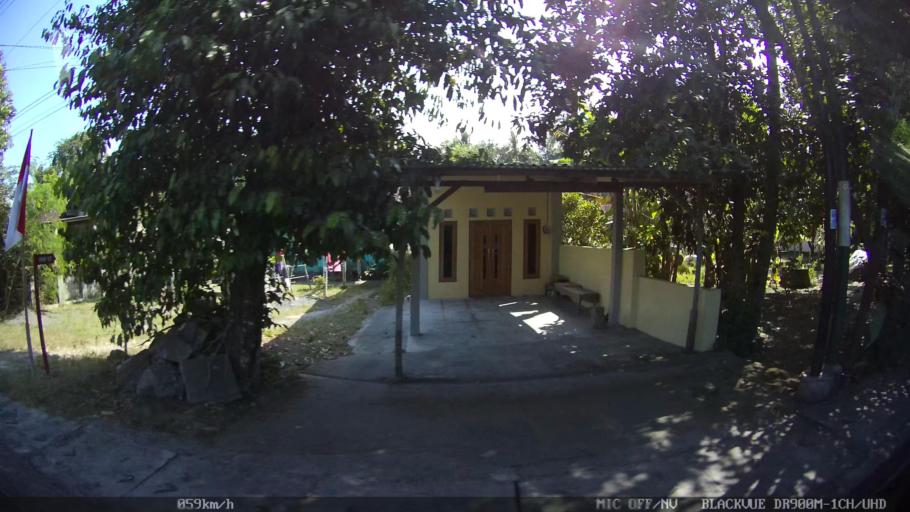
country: ID
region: Daerah Istimewa Yogyakarta
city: Srandakan
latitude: -7.9299
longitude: 110.2056
